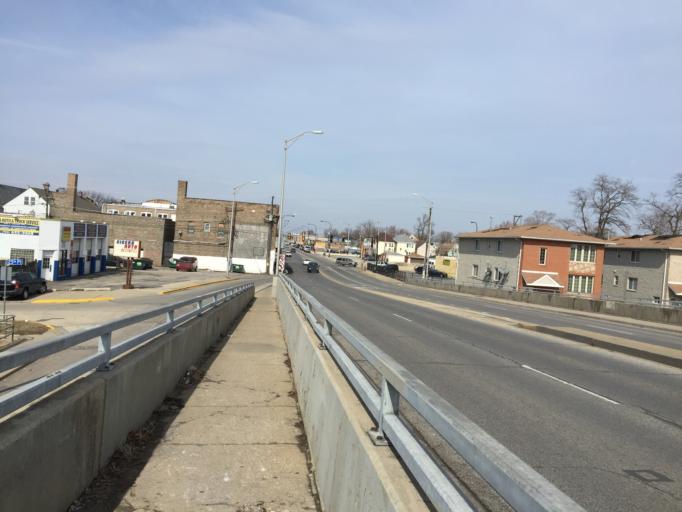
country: US
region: Illinois
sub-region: Cook County
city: Cicero
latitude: 41.8444
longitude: -87.7540
